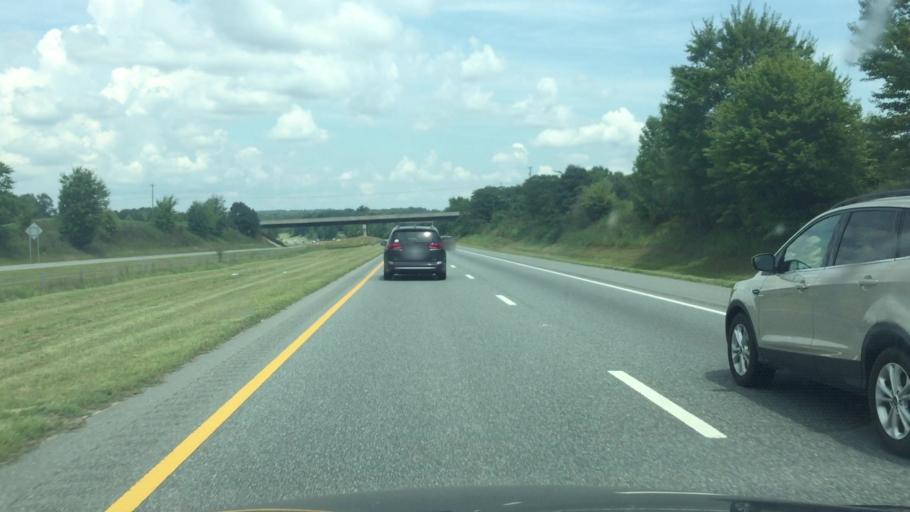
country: US
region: North Carolina
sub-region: Montgomery County
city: Biscoe
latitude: 35.4870
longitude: -79.7806
